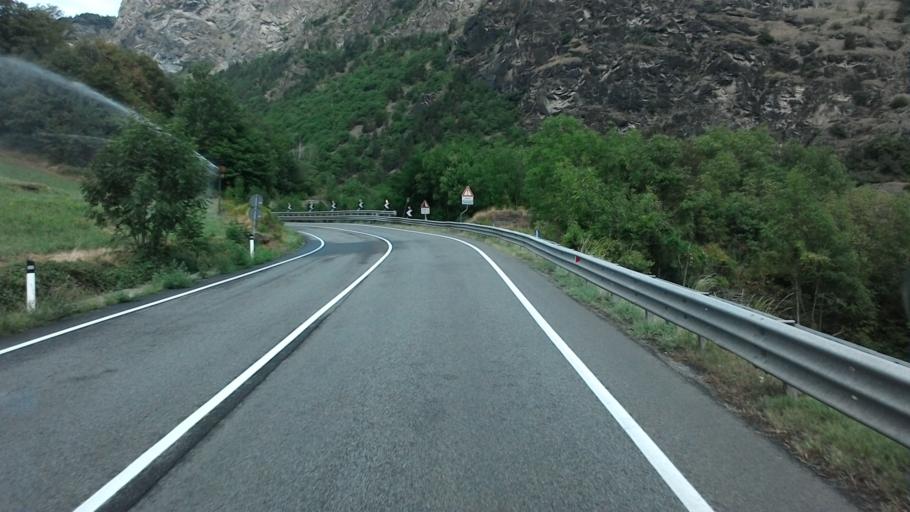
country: IT
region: Aosta Valley
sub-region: Valle d'Aosta
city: Introd
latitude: 45.7054
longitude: 7.1796
